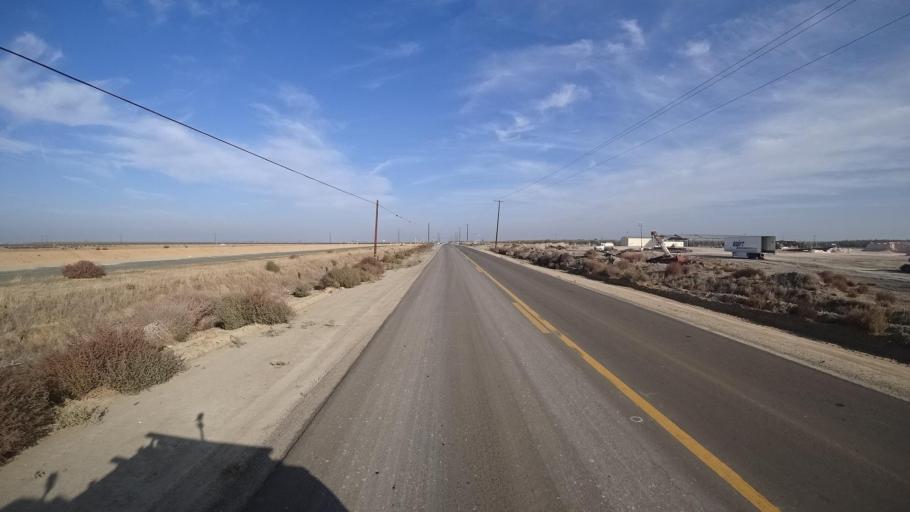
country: US
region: California
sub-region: Kern County
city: McFarland
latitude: 35.6430
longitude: -119.2045
